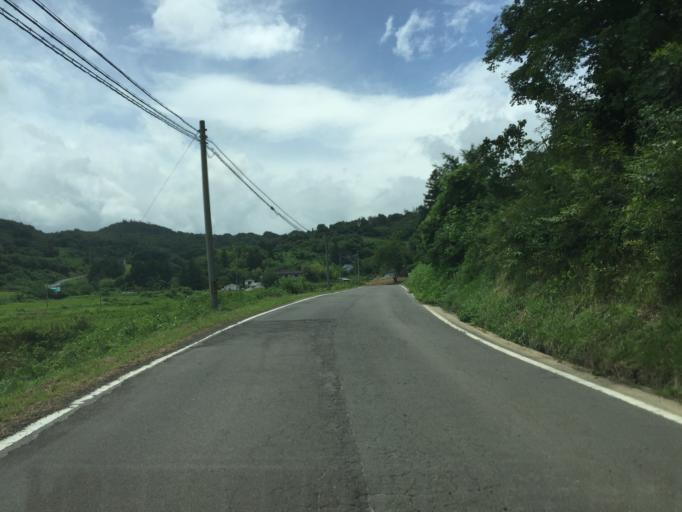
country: JP
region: Fukushima
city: Fukushima-shi
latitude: 37.6946
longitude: 140.4421
